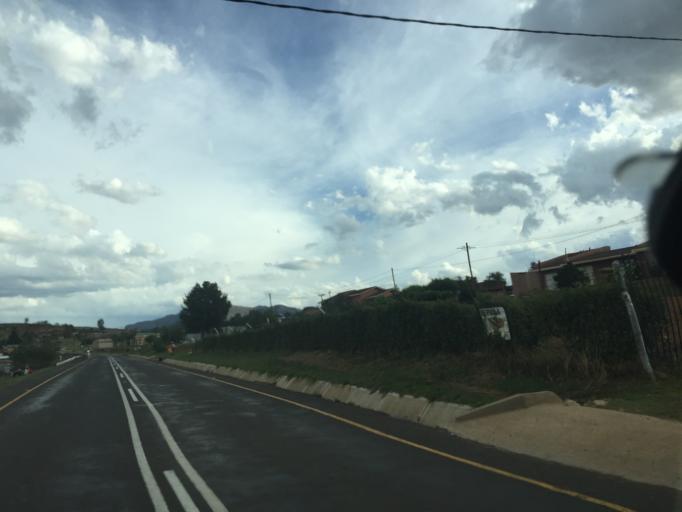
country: LS
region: Berea
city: Teyateyaneng
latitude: -29.1327
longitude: 27.9870
